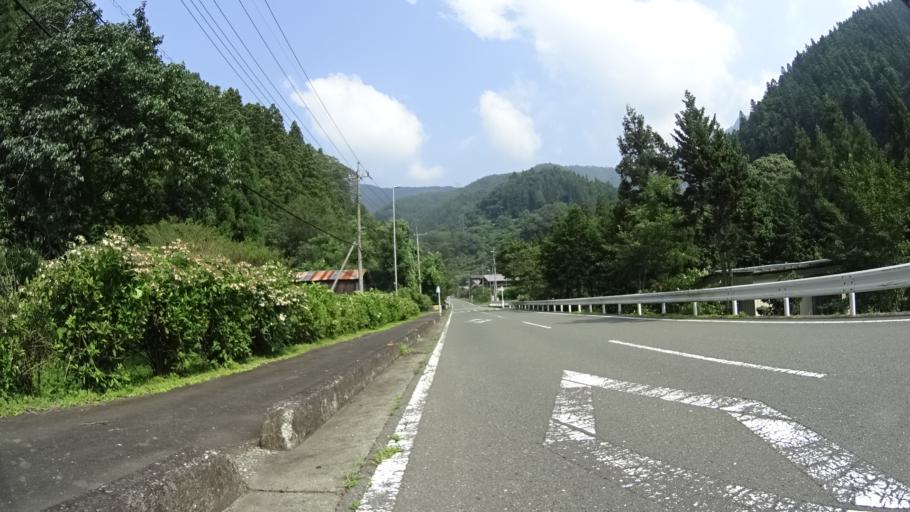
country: JP
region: Gunma
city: Tomioka
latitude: 36.0539
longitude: 138.8620
